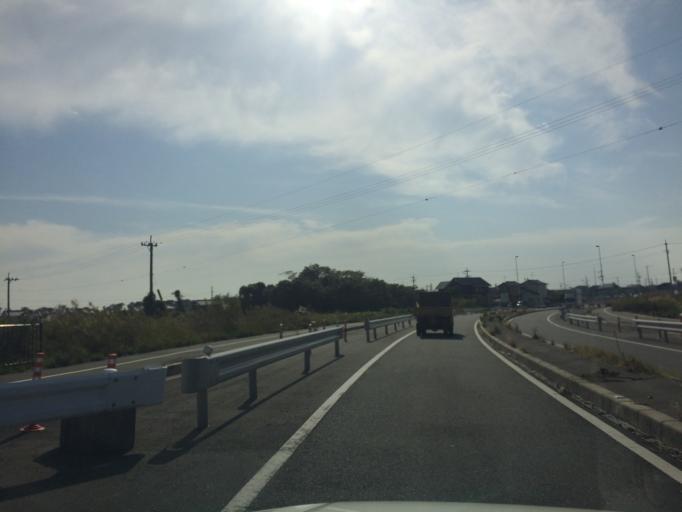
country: JP
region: Shizuoka
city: Fujieda
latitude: 34.7665
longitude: 138.2764
